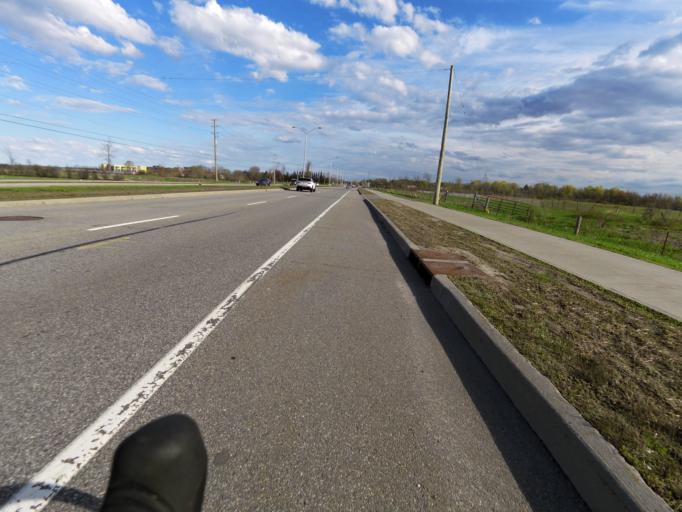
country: CA
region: Ontario
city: Ottawa
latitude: 45.2938
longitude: -75.6749
